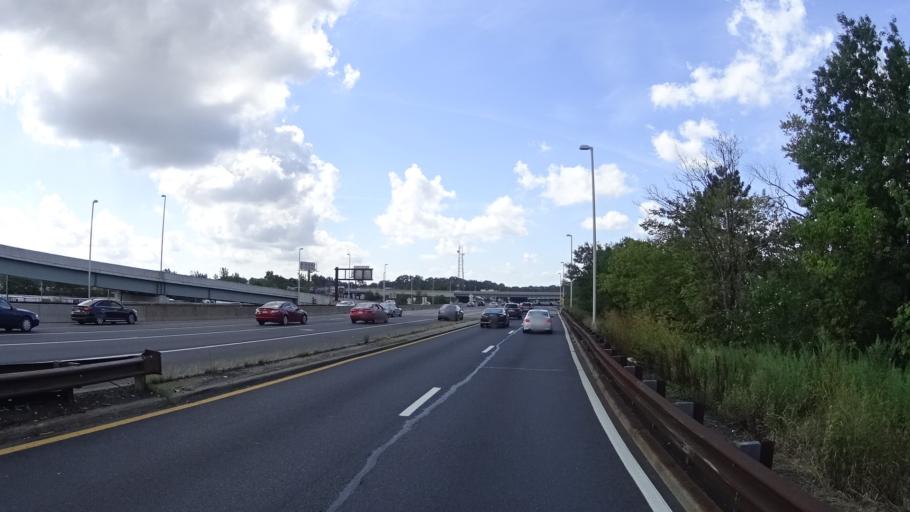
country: US
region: New Jersey
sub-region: Union County
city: Hillside
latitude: 40.7085
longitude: -74.2454
